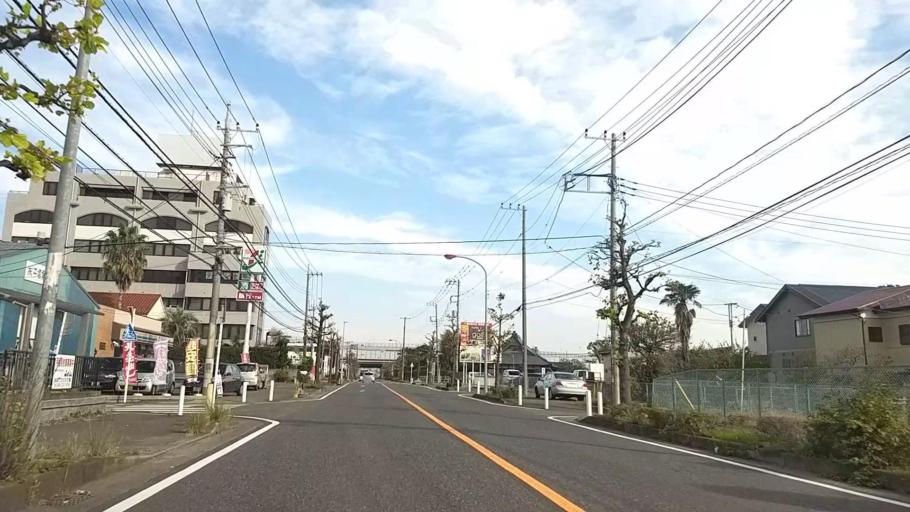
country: JP
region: Kanagawa
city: Atsugi
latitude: 35.4199
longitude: 139.3649
